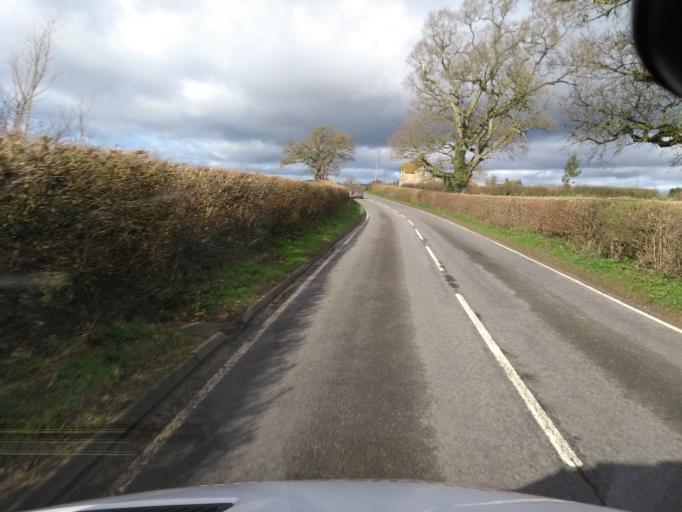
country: GB
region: England
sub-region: Somerset
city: Milborne Port
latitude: 50.9174
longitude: -2.4500
